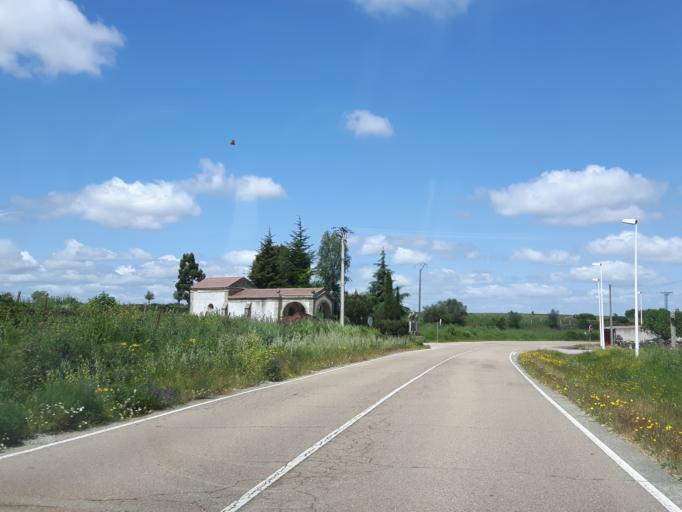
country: ES
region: Castille and Leon
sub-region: Provincia de Salamanca
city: Villar de la Yegua
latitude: 40.7236
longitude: -6.7048
